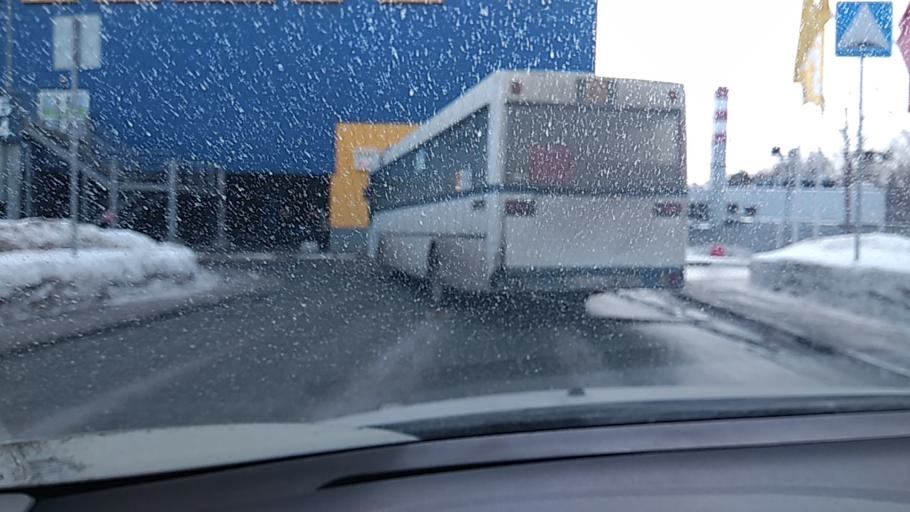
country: RU
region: Sverdlovsk
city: Shirokaya Rechka
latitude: 56.8251
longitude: 60.5015
